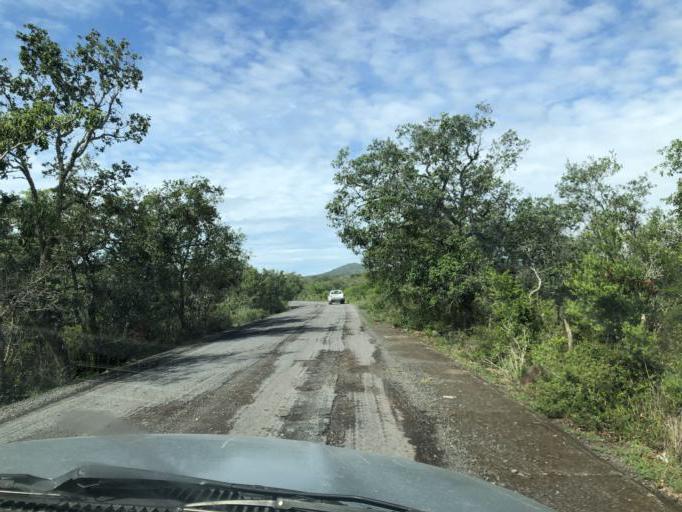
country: MX
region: Veracruz
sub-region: Alto Lucero de Gutierrez Barrios
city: Palma Sola
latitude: 19.7921
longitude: -96.5513
